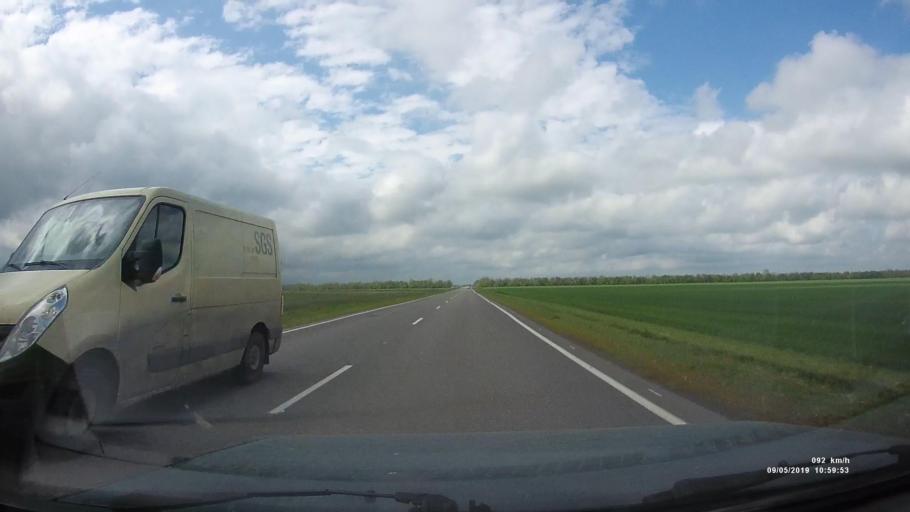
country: RU
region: Rostov
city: Peshkovo
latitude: 46.8554
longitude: 39.2306
